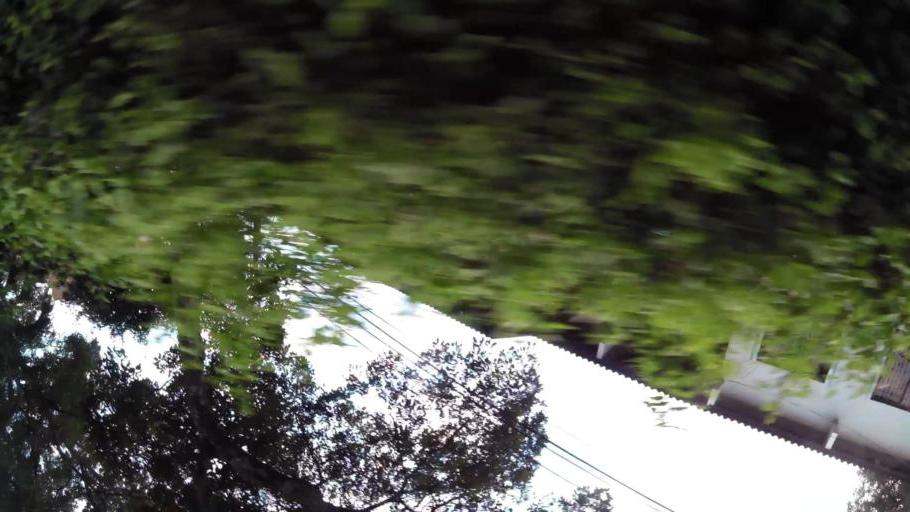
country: CO
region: Valle del Cauca
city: Cali
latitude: 3.4667
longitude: -76.5154
